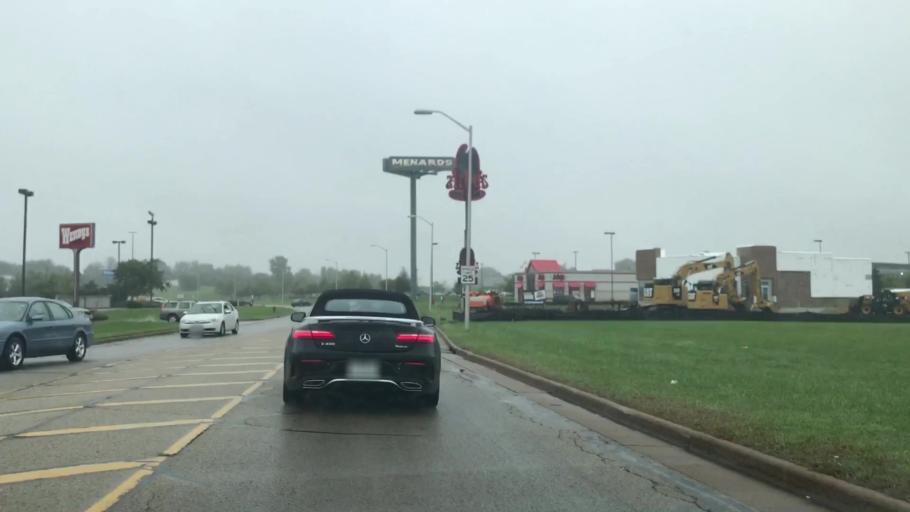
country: US
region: Wisconsin
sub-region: Dodge County
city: Beaver Dam
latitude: 43.4863
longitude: -88.8099
